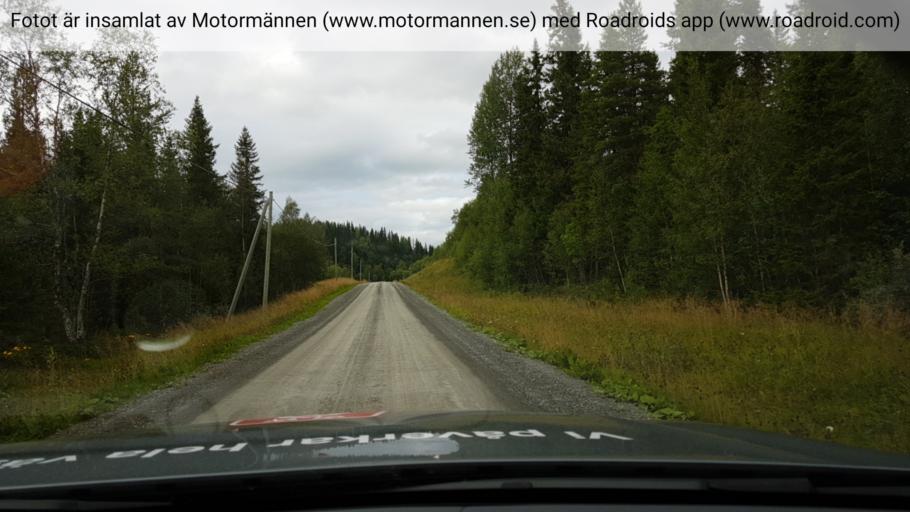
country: SE
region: Jaemtland
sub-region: Krokoms Kommun
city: Valla
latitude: 63.7139
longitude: 13.5301
